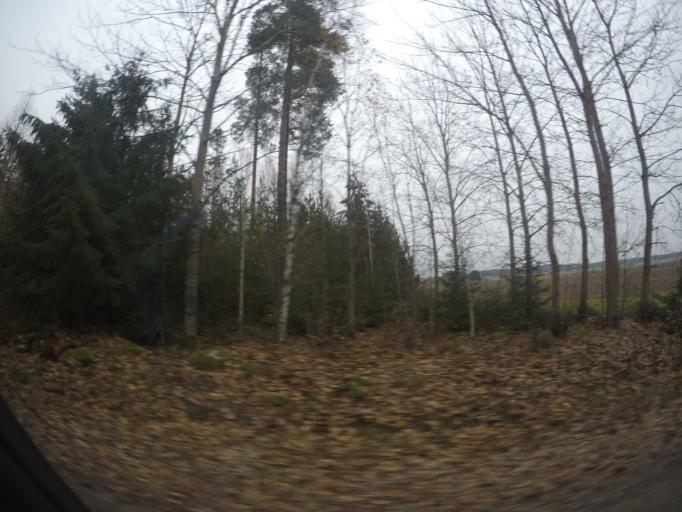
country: SE
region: Vaestmanland
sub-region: Kopings Kommun
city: Koping
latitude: 59.6012
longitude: 16.0761
